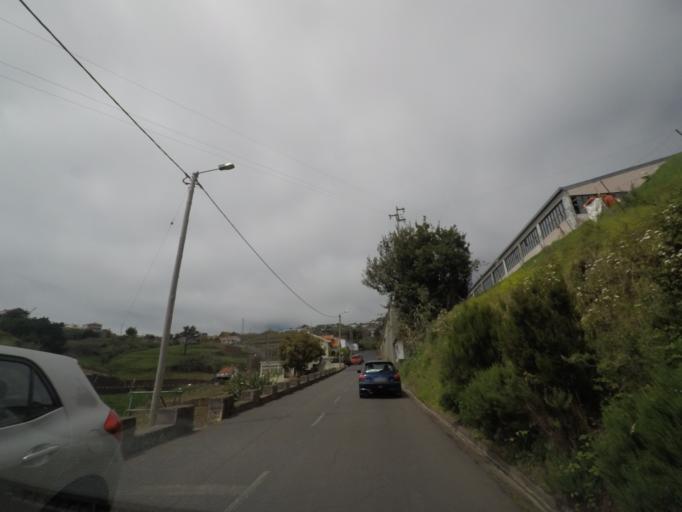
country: PT
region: Madeira
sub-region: Calheta
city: Arco da Calheta
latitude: 32.7051
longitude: -17.1128
